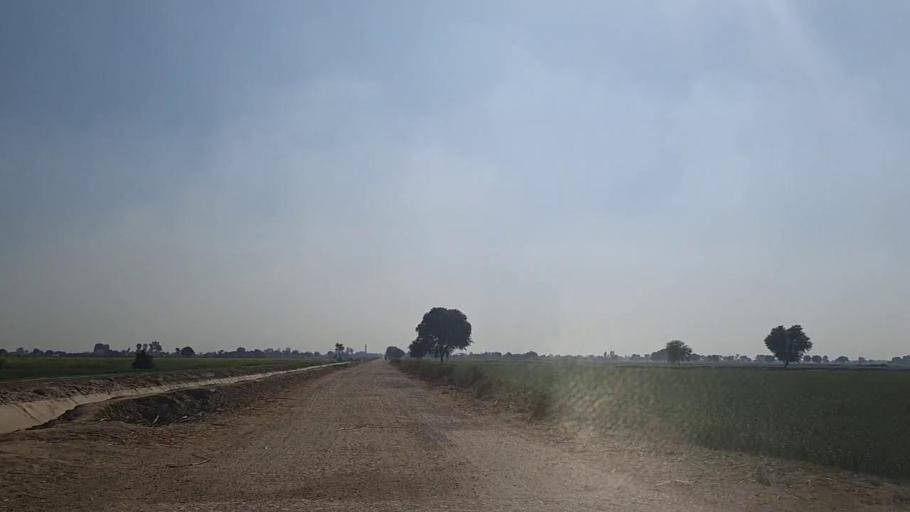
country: PK
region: Sindh
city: Shahpur Chakar
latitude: 26.2004
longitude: 68.5837
